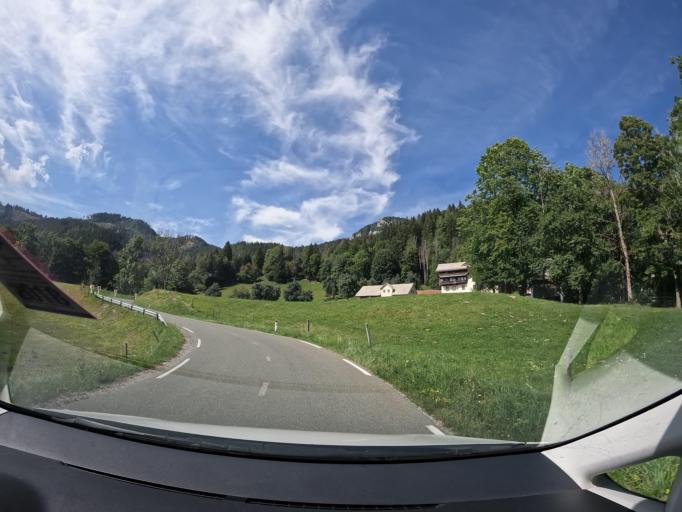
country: AT
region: Carinthia
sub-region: Politischer Bezirk Feldkirchen
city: Glanegg
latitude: 46.7451
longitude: 14.1698
